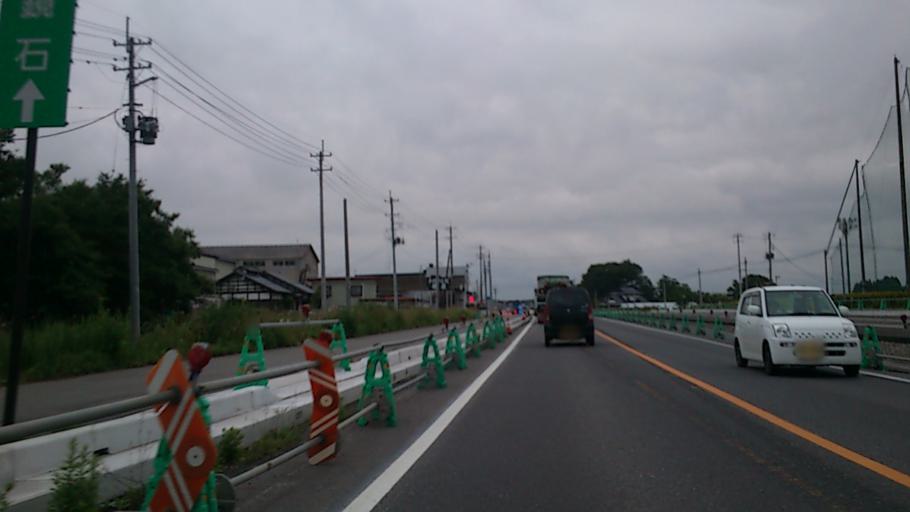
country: JP
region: Fukushima
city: Sukagawa
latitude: 37.2635
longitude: 140.3506
